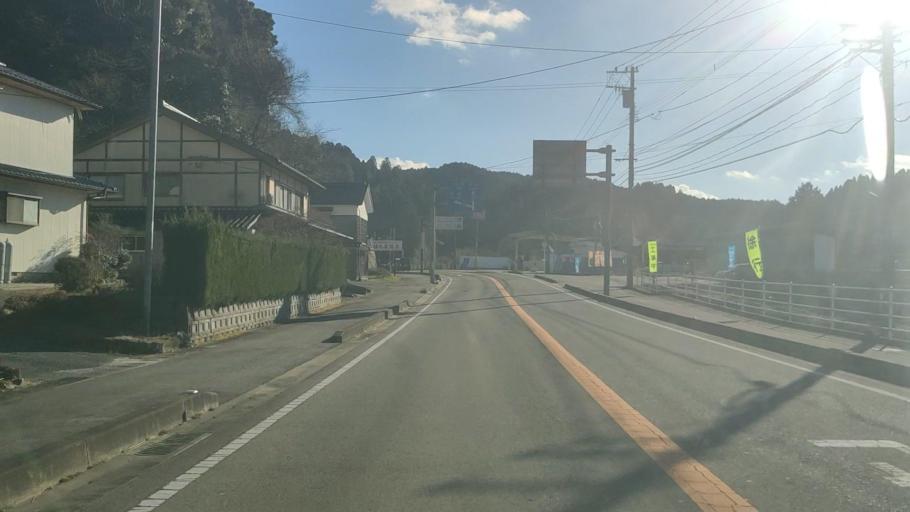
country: JP
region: Saga Prefecture
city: Kanzakimachi-kanzaki
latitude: 33.4237
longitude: 130.2775
